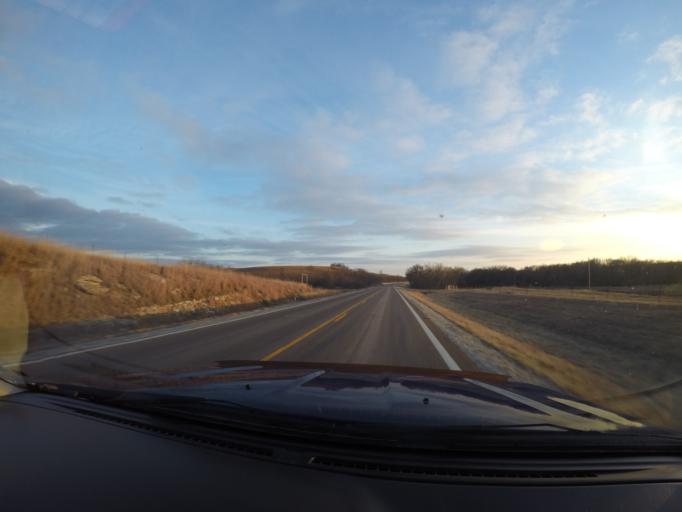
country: US
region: Kansas
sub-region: Chase County
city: Cottonwood Falls
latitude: 38.4728
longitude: -96.5554
